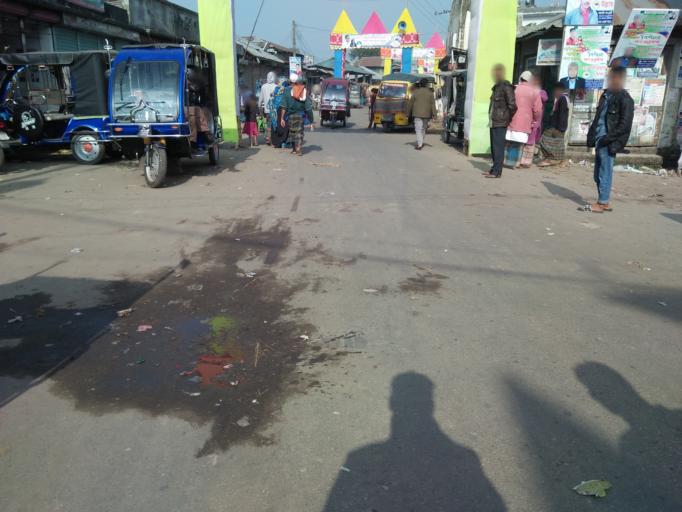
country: BD
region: Khulna
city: Uttar Char Fasson
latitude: 22.1910
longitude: 90.6752
